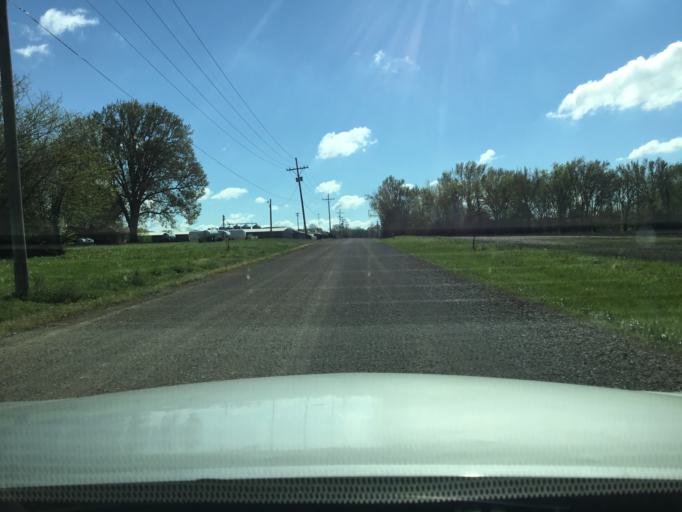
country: US
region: Kansas
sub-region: Allen County
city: Iola
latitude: 37.9285
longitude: -95.4162
